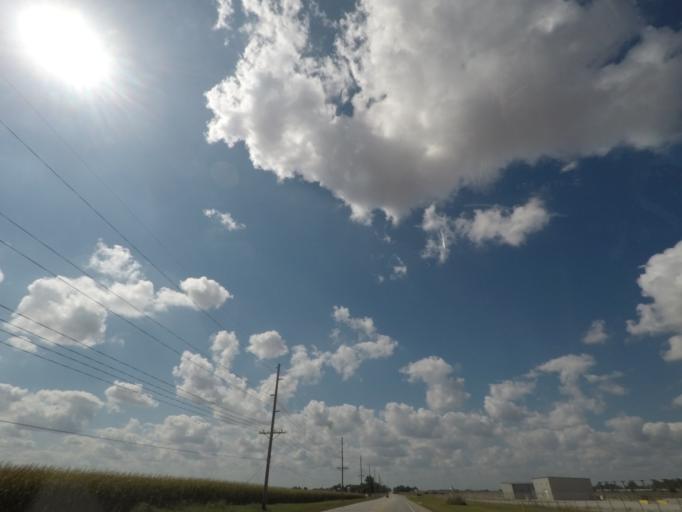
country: US
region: Iowa
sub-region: Story County
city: Nevada
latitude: 42.0231
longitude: -93.5159
